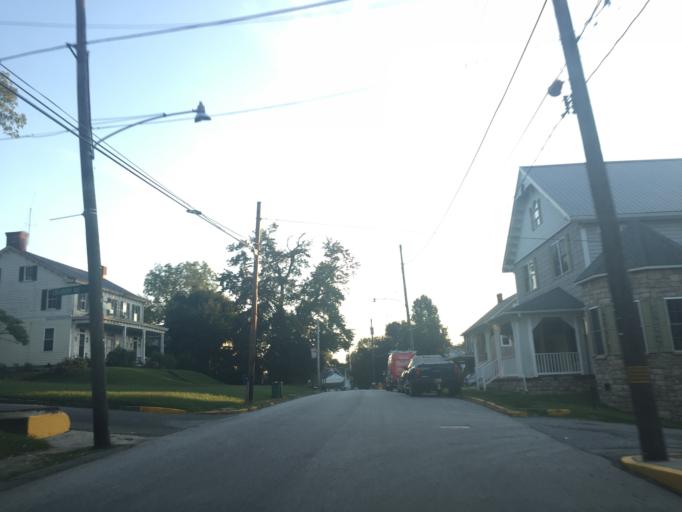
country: US
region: Pennsylvania
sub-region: York County
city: Susquehanna Trails
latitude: 39.7253
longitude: -76.3305
